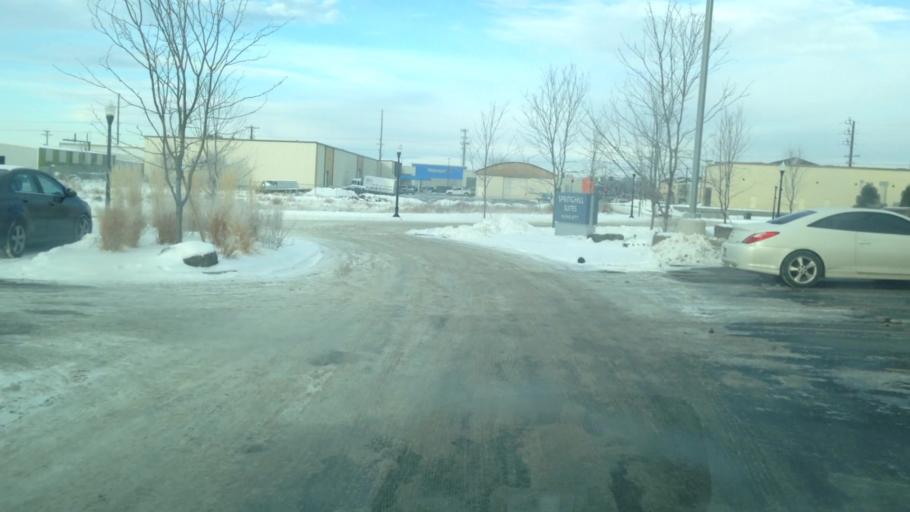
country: US
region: Idaho
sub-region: Bonneville County
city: Idaho Falls
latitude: 43.4914
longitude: -112.0470
